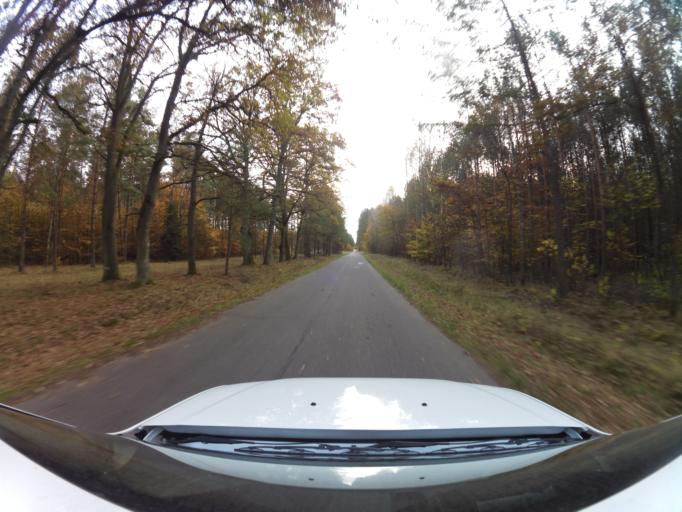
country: PL
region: West Pomeranian Voivodeship
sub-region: Powiat goleniowski
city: Nowogard
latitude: 53.8036
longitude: 15.1271
